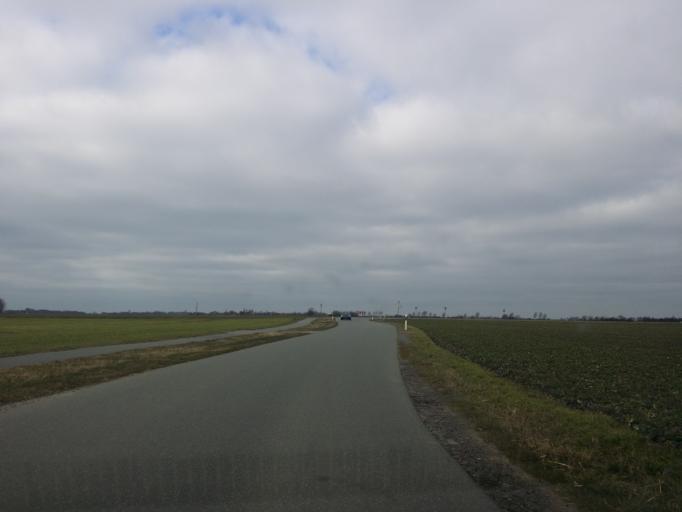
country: DE
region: Schleswig-Holstein
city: Grossenbrode
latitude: 54.4830
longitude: 11.0569
